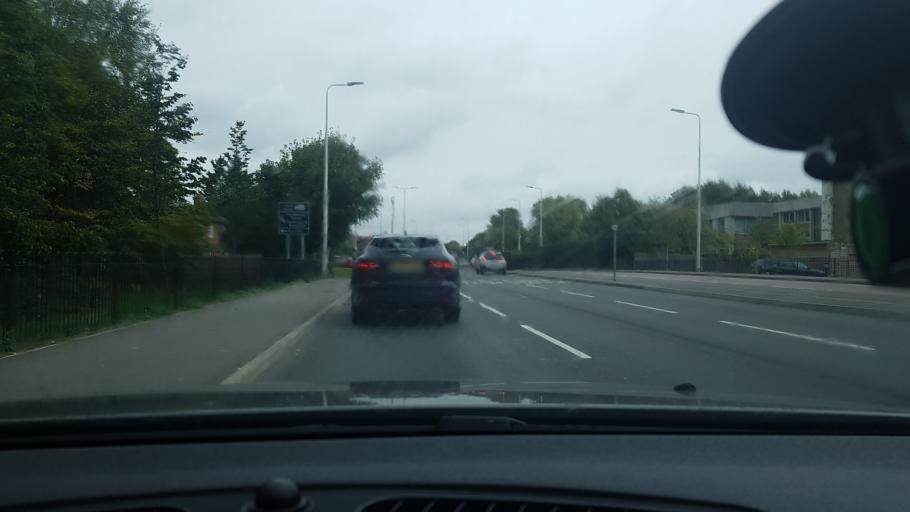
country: GB
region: England
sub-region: West Berkshire
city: Newbury
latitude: 51.4053
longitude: -1.3179
